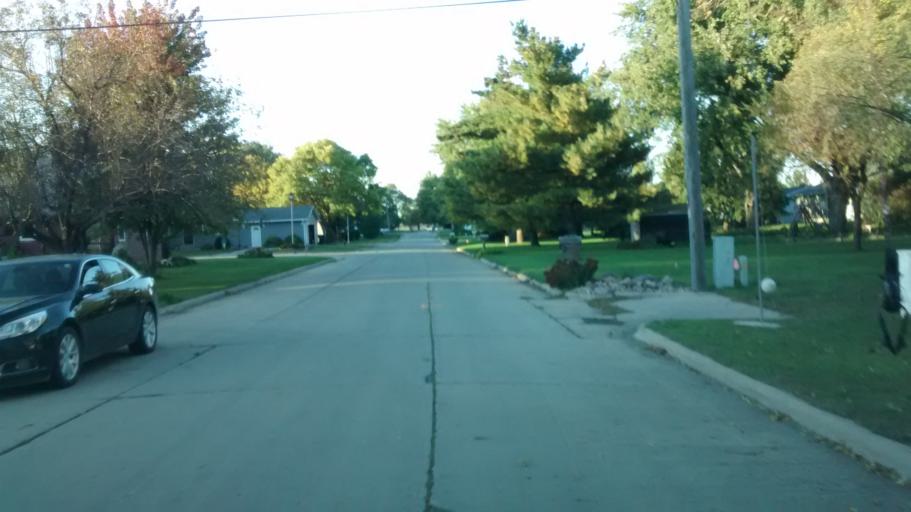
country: US
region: Iowa
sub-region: Woodbury County
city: Moville
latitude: 42.4891
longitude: -96.0675
